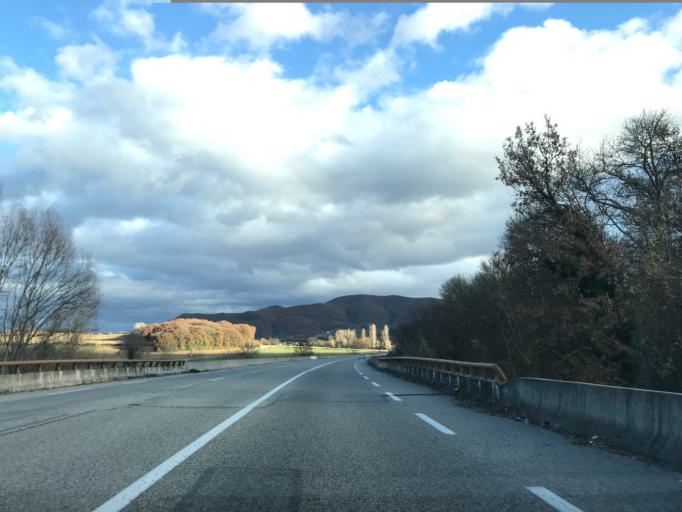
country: FR
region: Rhone-Alpes
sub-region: Departement de l'Ardeche
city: Saint-Julien-en-Saint-Alban
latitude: 44.7112
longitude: 4.7124
